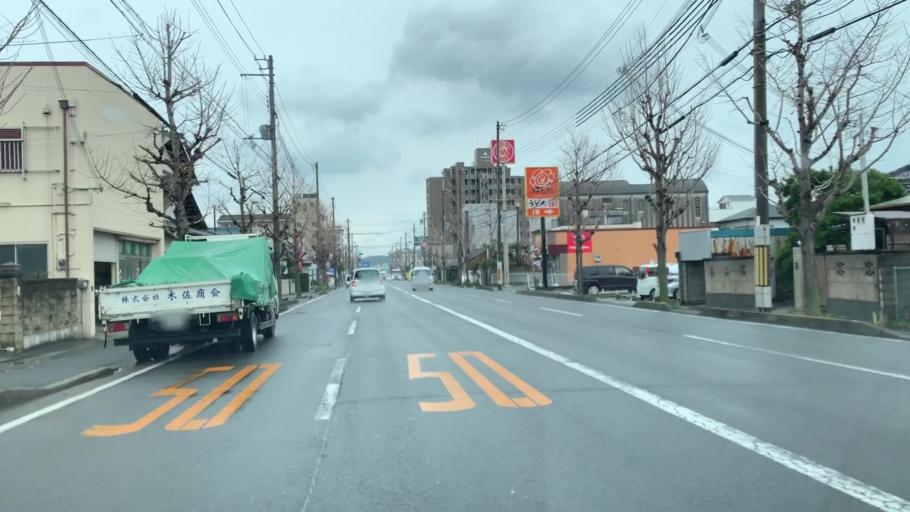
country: JP
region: Wakayama
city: Wakayama-shi
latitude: 34.2228
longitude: 135.1595
